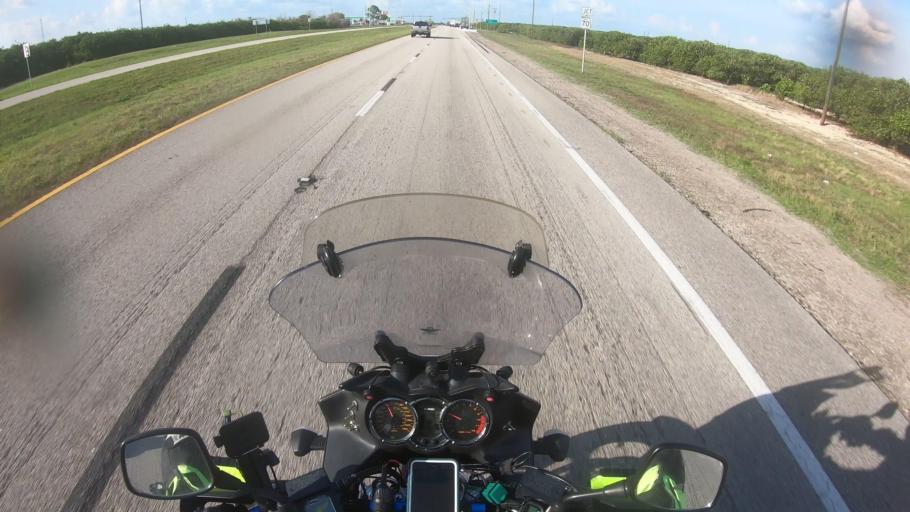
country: US
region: Florida
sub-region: Highlands County
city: Placid Lakes
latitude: 27.2053
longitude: -81.3279
